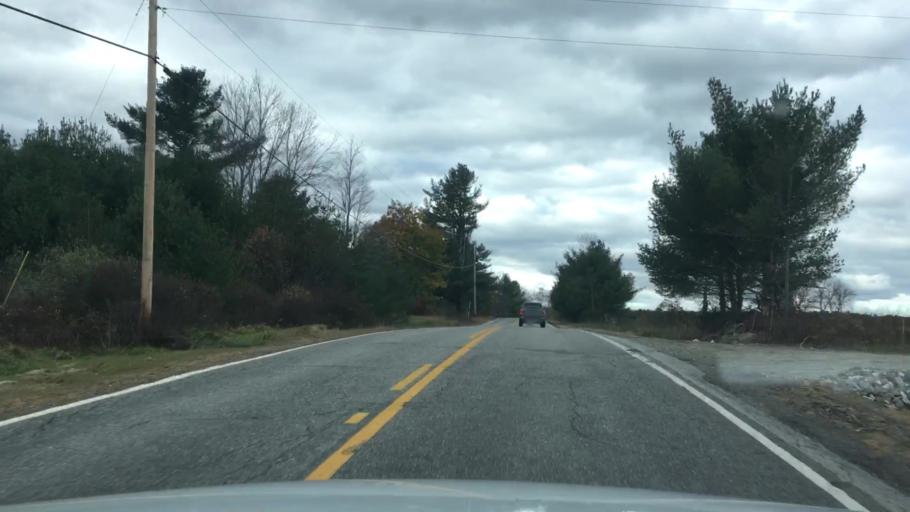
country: US
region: Maine
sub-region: Sagadahoc County
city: Richmond
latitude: 44.1097
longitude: -69.9060
